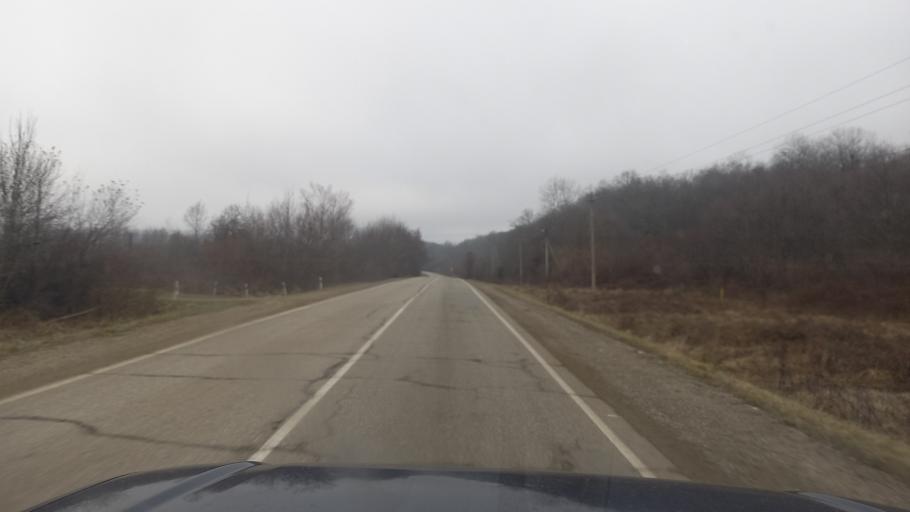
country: RU
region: Krasnodarskiy
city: Neftegorsk
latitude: 44.2864
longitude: 39.8066
